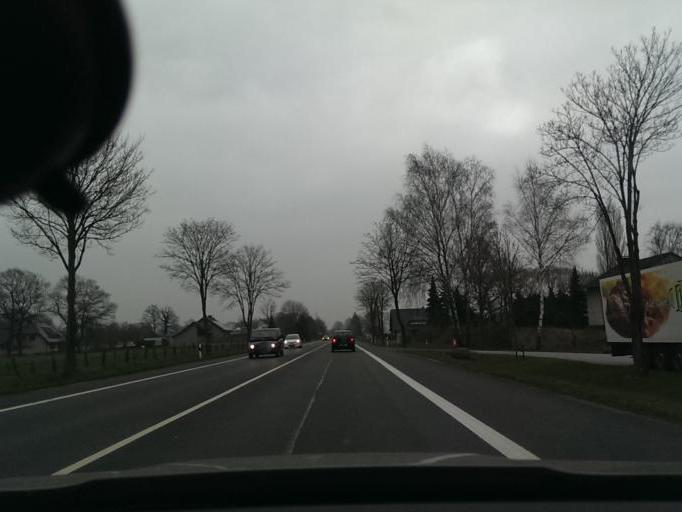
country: DE
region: North Rhine-Westphalia
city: Rietberg
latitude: 51.7815
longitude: 8.4766
